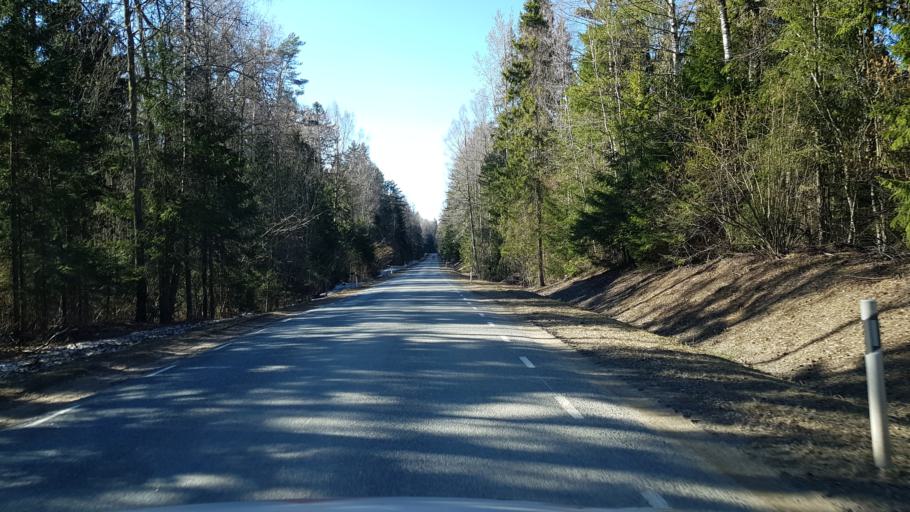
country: EE
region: Laeaene-Virumaa
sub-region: Vinni vald
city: Vinni
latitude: 59.2656
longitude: 26.6730
